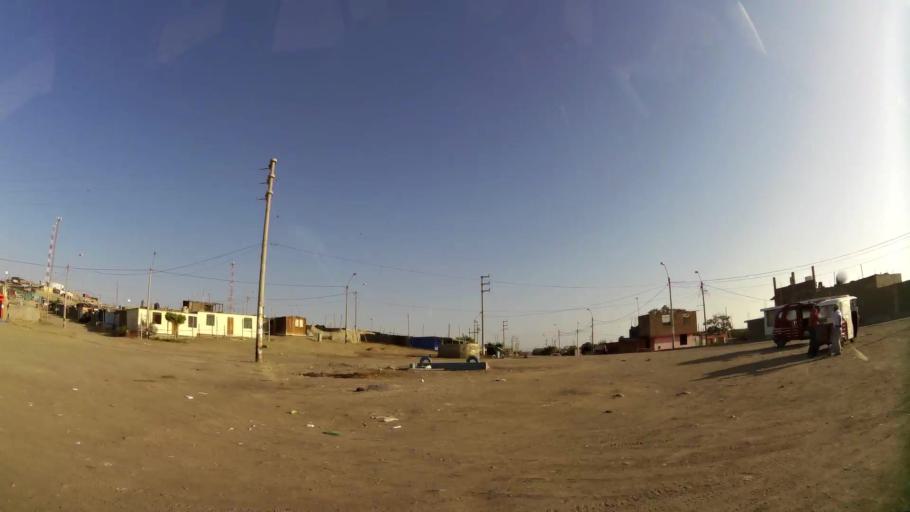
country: PE
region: Ica
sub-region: Provincia de Pisco
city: Villa Tupac Amaru
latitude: -13.7094
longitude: -76.1455
